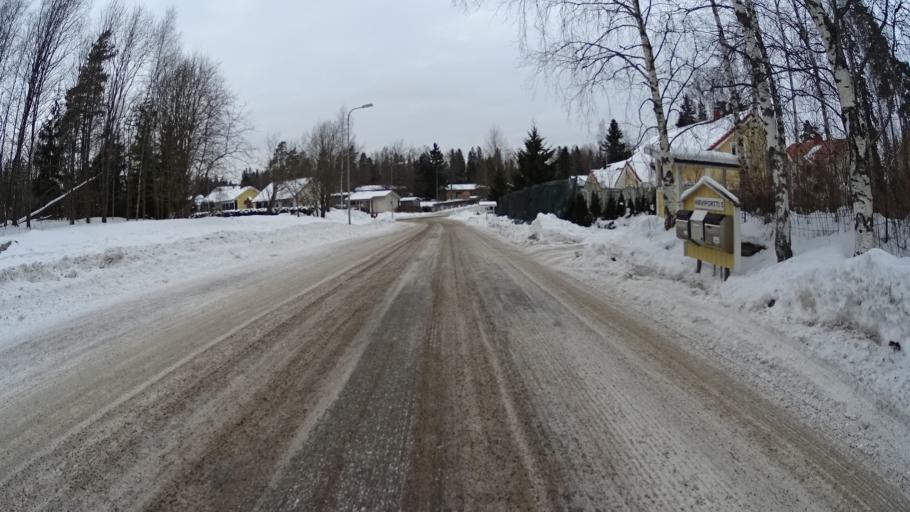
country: FI
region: Uusimaa
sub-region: Helsinki
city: Espoo
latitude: 60.2184
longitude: 24.6305
